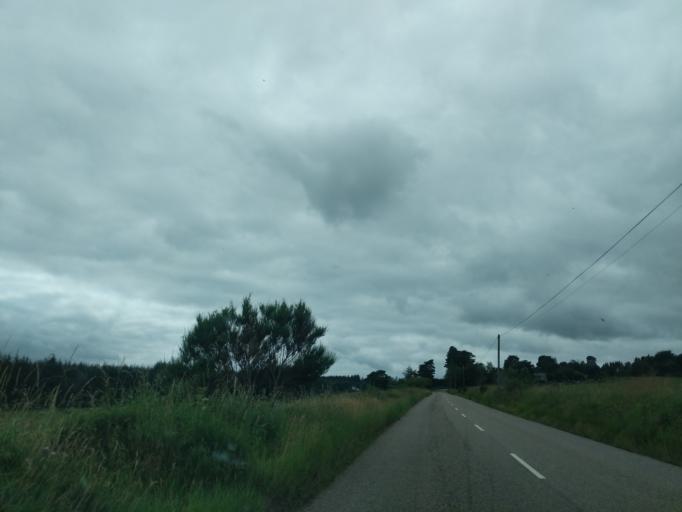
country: GB
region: Scotland
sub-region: Moray
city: Rothes
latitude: 57.4879
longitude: -3.2459
